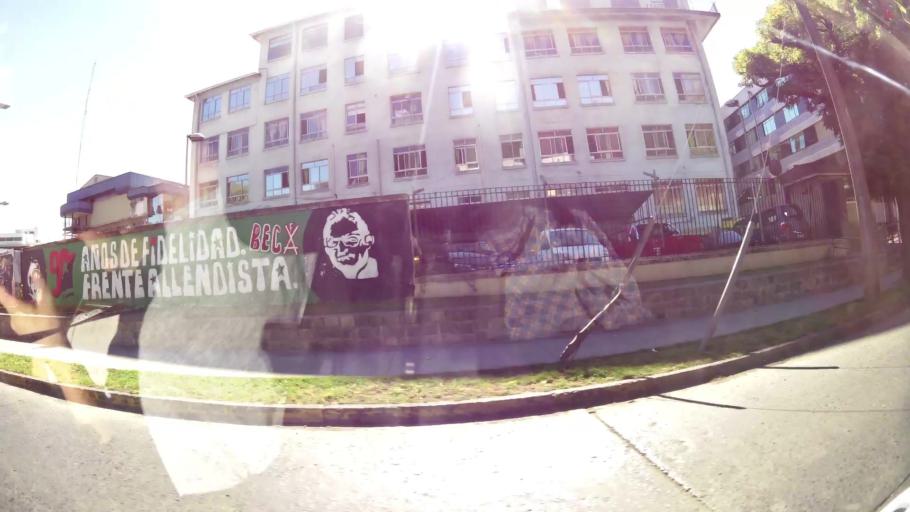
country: CL
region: Biobio
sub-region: Provincia de Concepcion
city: Concepcion
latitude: -36.8252
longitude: -73.0371
